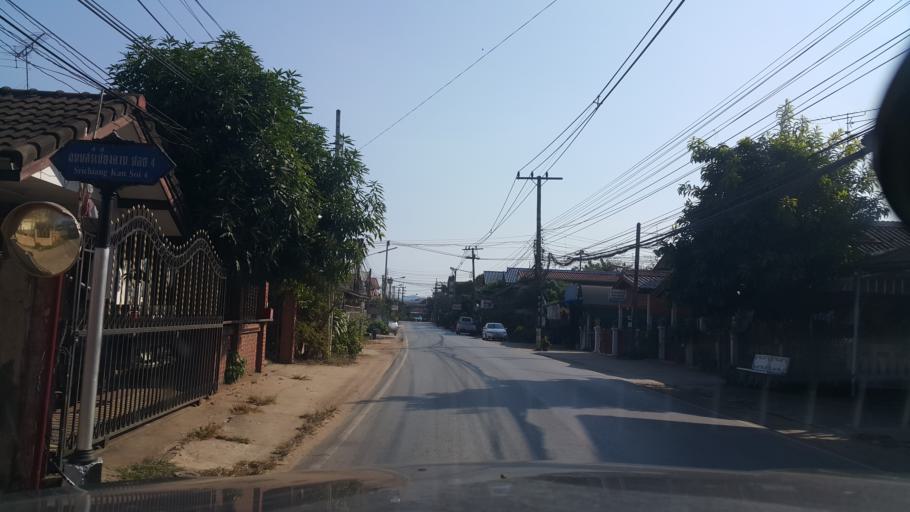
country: TH
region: Loei
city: Chiang Khan
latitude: 17.8920
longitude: 101.6504
